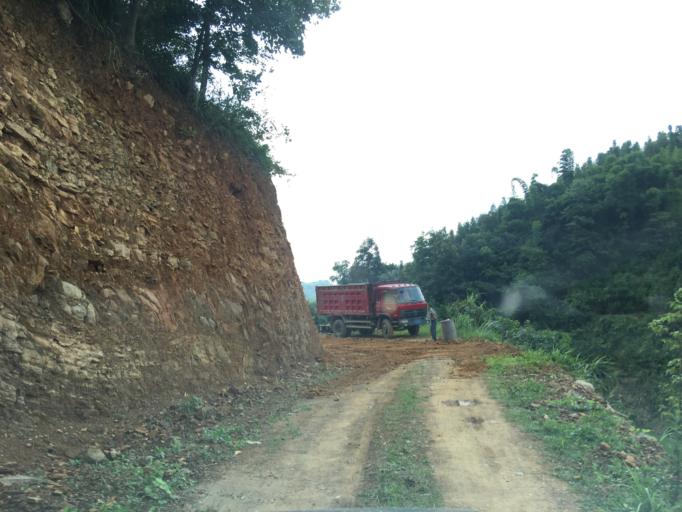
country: CN
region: Guangxi Zhuangzu Zizhiqu
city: Xinzhou
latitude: 24.8688
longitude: 105.8651
